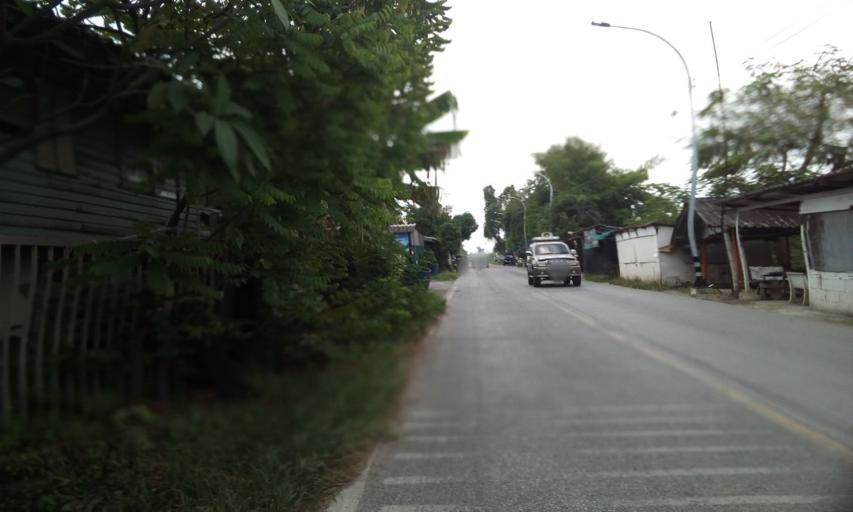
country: TH
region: Pathum Thani
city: Ban Rangsit
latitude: 14.0359
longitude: 100.7791
